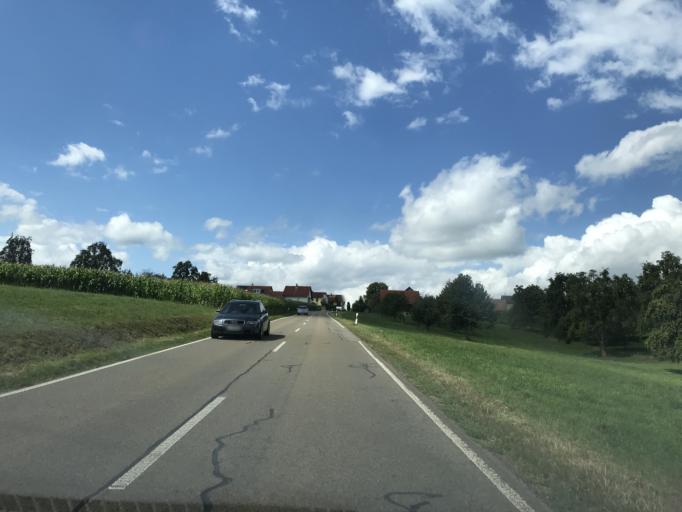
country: DE
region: Baden-Wuerttemberg
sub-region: Freiburg Region
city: Maulburg
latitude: 47.6108
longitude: 7.7653
